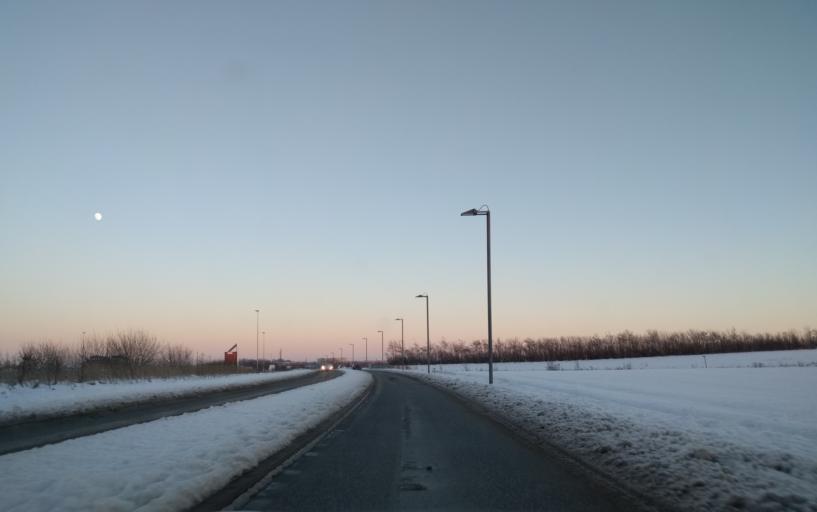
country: DK
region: North Denmark
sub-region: Alborg Kommune
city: Gistrup
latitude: 57.0129
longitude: 9.9697
